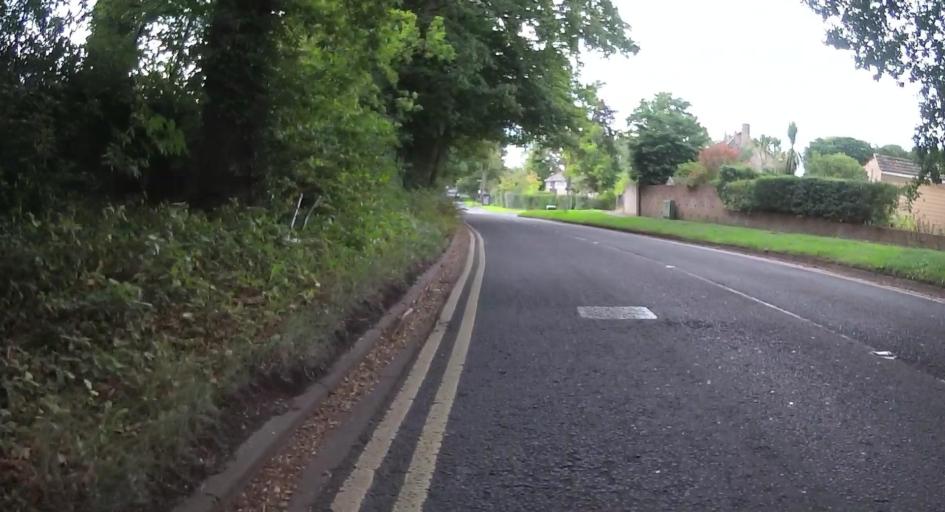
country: GB
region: England
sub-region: Surrey
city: Windlesham
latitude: 51.3481
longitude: -0.6651
